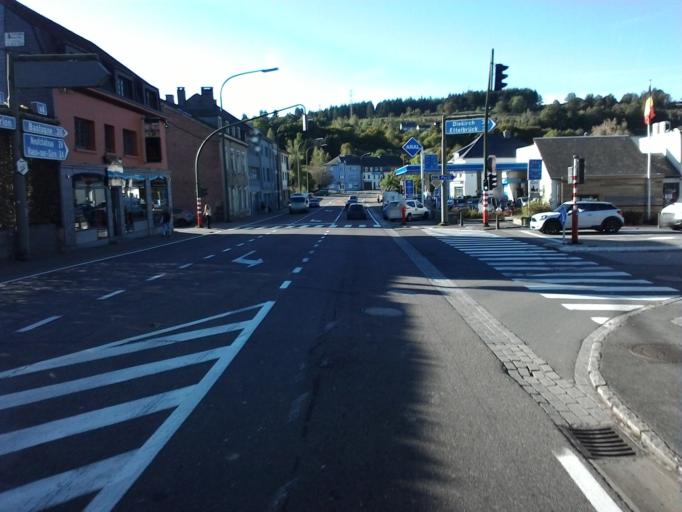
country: BE
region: Wallonia
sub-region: Province du Luxembourg
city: Martelange
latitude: 49.8330
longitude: 5.7407
